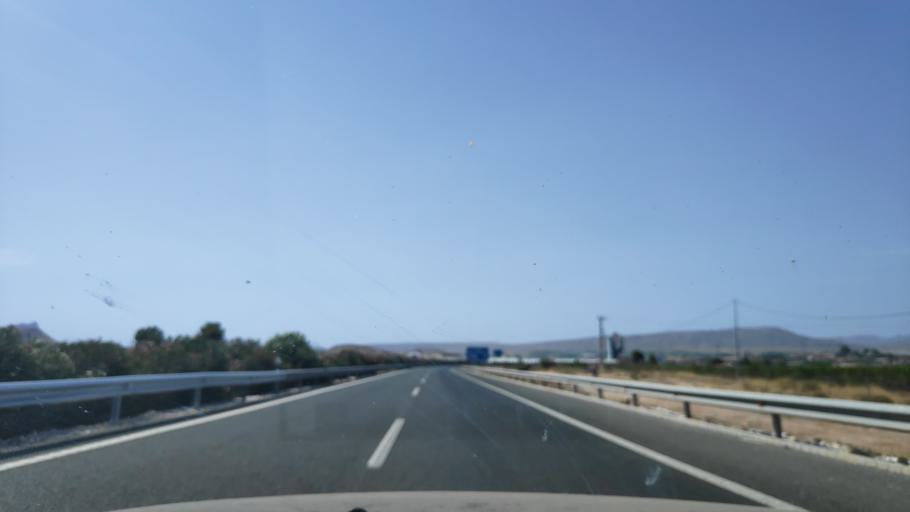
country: ES
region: Murcia
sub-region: Murcia
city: Blanca
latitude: 38.2055
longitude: -1.3478
